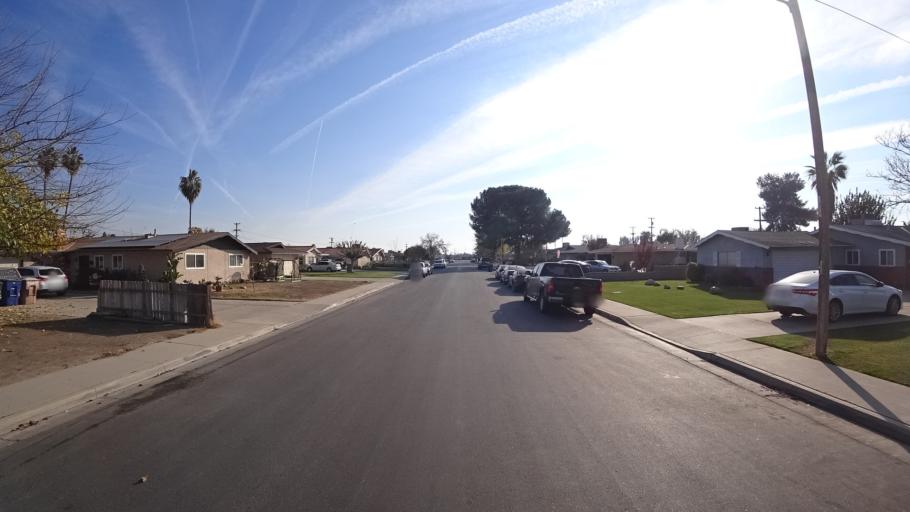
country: US
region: California
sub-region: Kern County
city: Bakersfield
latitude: 35.3222
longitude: -119.0243
